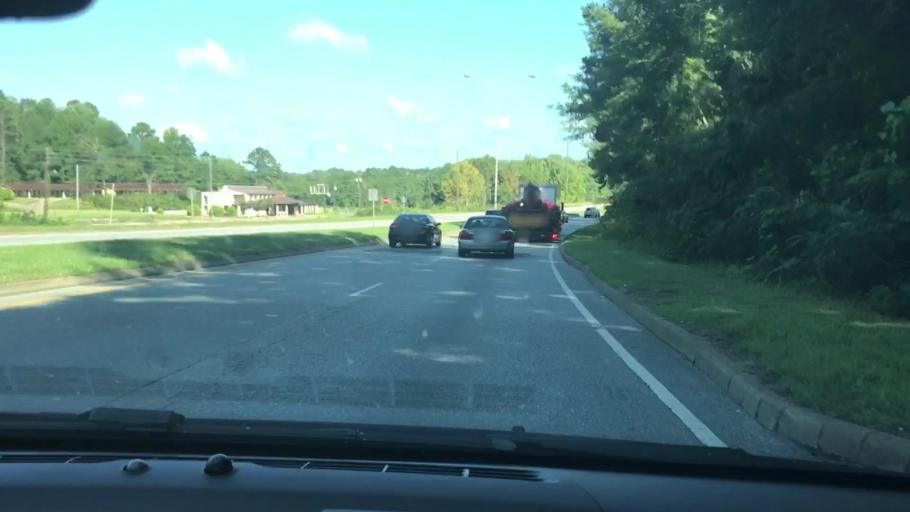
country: US
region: Alabama
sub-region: Barbour County
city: Eufaula
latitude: 31.9050
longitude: -85.1484
